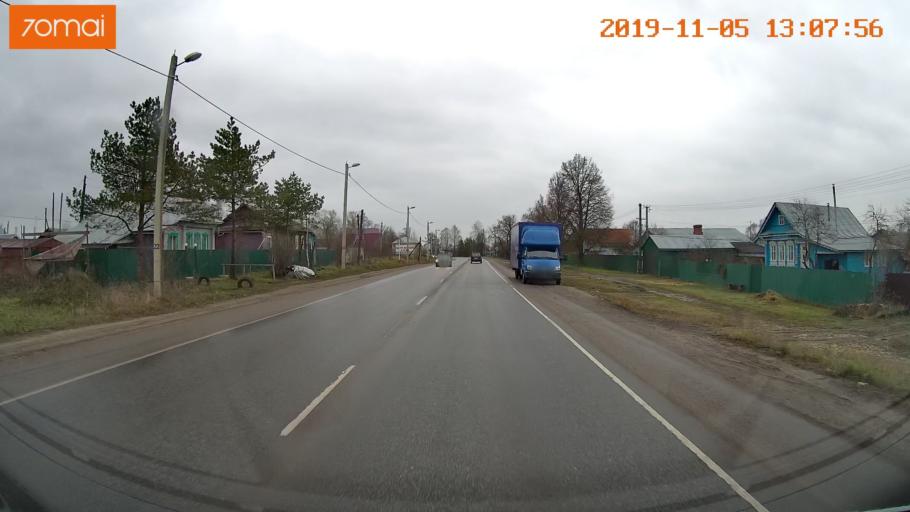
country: RU
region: Ivanovo
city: Kitovo
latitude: 56.8656
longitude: 41.2864
